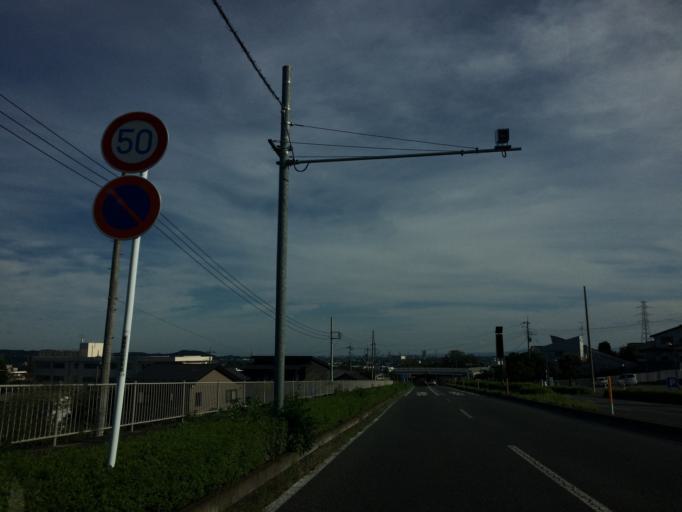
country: JP
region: Gunma
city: Shibukawa
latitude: 36.4865
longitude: 138.9988
